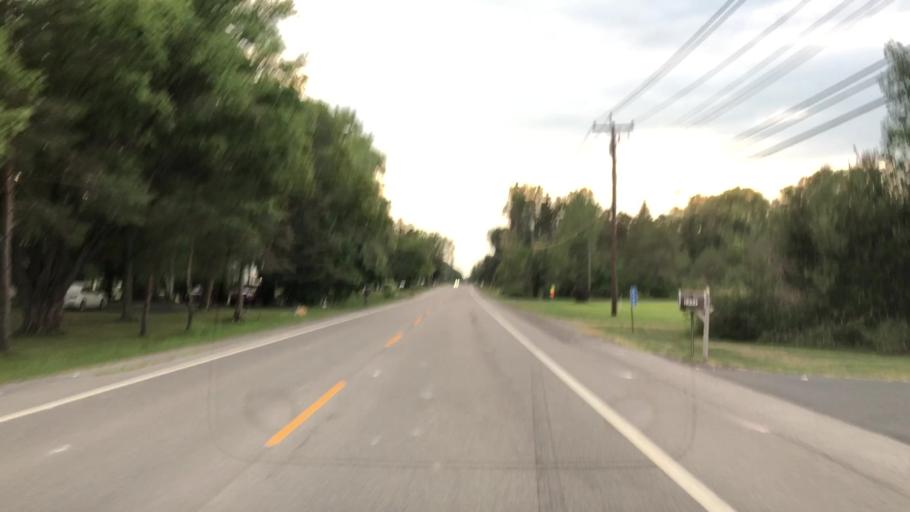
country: US
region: New York
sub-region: Erie County
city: Elma Center
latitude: 42.8391
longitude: -78.6520
